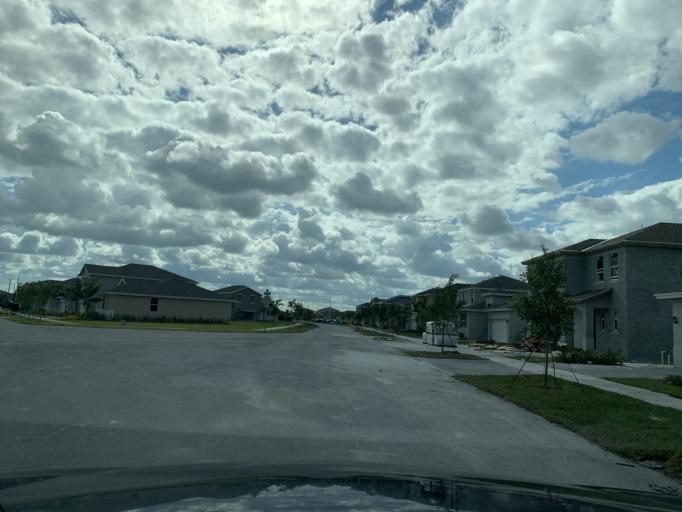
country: US
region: Florida
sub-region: Miami-Dade County
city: Naranja
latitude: 25.5122
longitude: -80.4090
